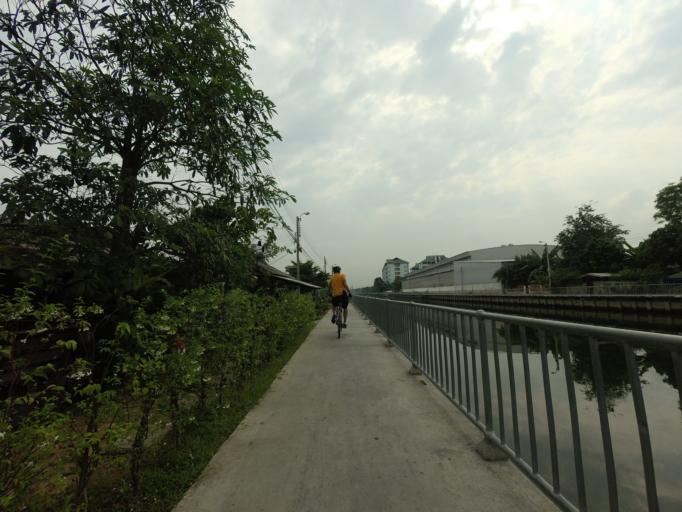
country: TH
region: Bangkok
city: Suan Luang
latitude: 13.7241
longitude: 100.6747
